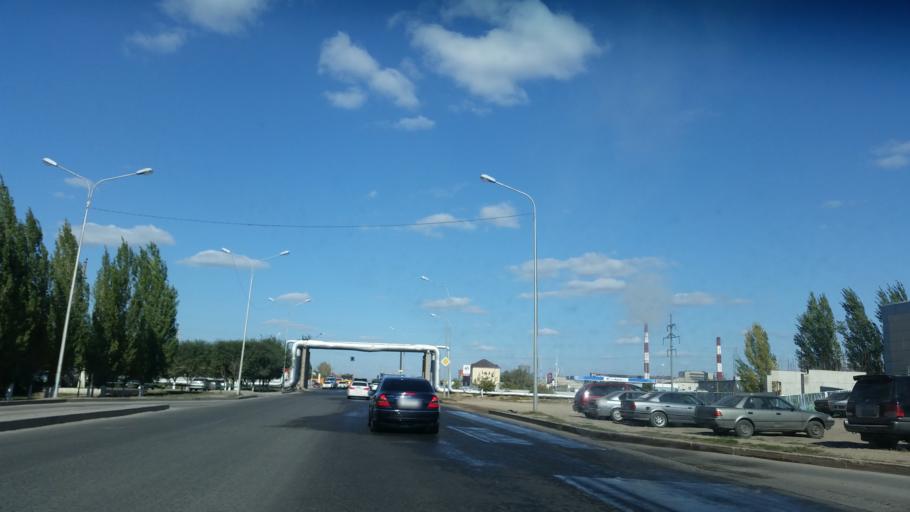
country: KZ
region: Astana Qalasy
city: Astana
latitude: 51.1778
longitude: 71.4874
